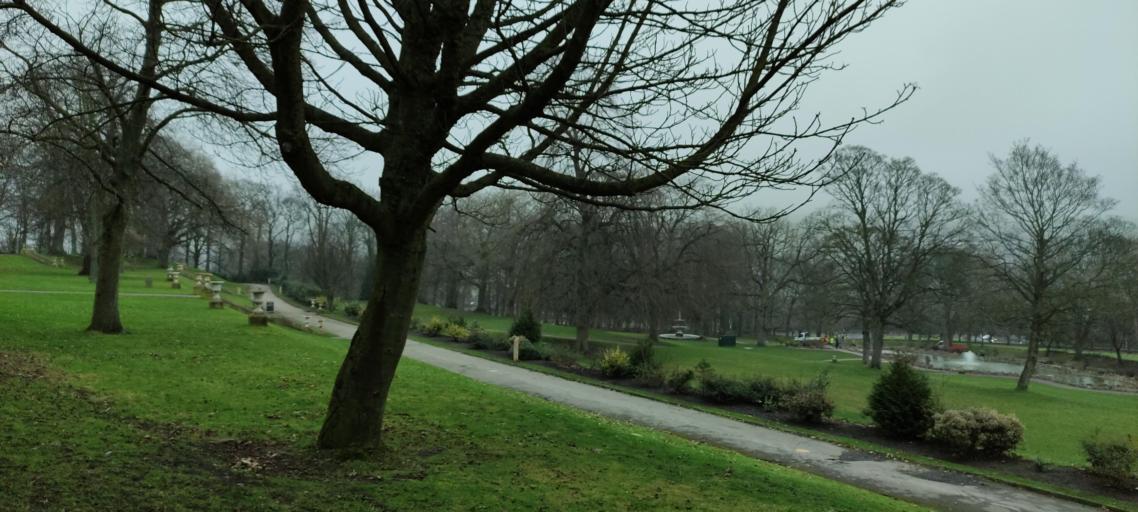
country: GB
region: England
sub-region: Bradford
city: Keighley
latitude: 53.8744
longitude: -1.9132
